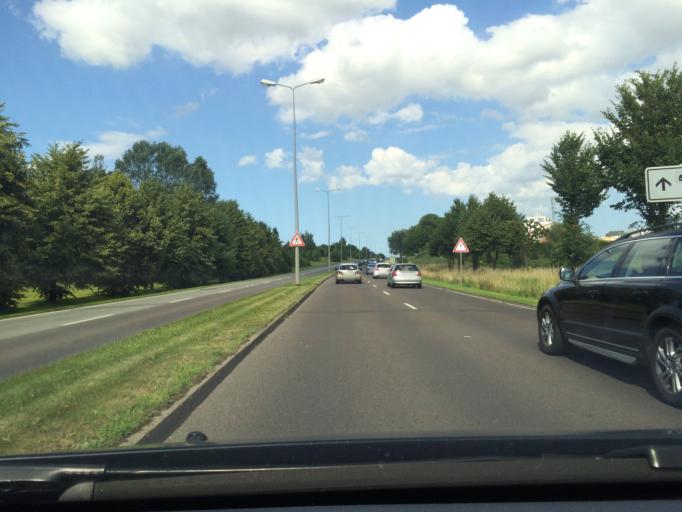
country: DE
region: Mecklenburg-Vorpommern
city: Dierkow-Neu
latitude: 54.0955
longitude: 12.1683
